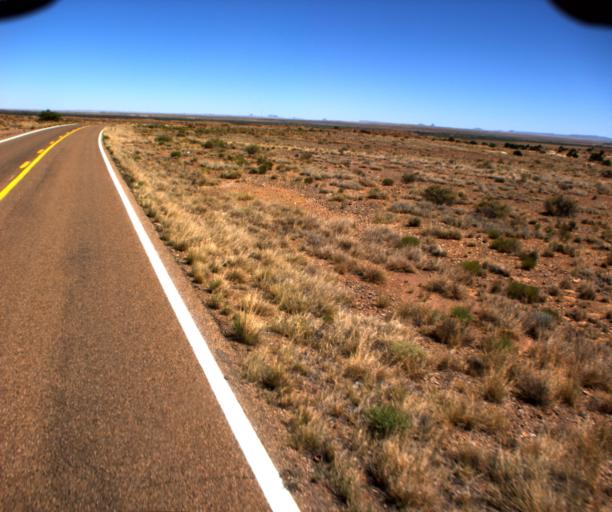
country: US
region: Arizona
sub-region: Navajo County
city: Winslow
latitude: 34.9590
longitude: -110.6474
